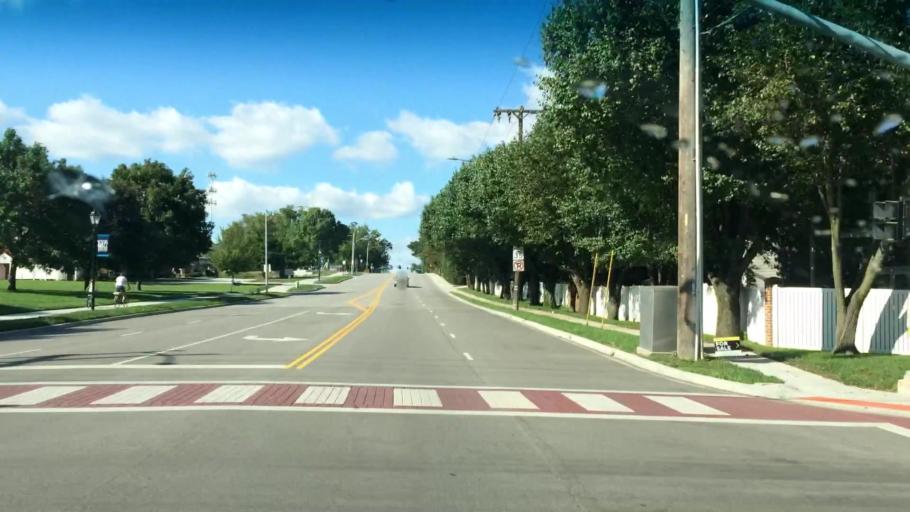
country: US
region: Kansas
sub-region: Johnson County
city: Prairie Village
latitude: 38.9860
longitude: -94.6304
